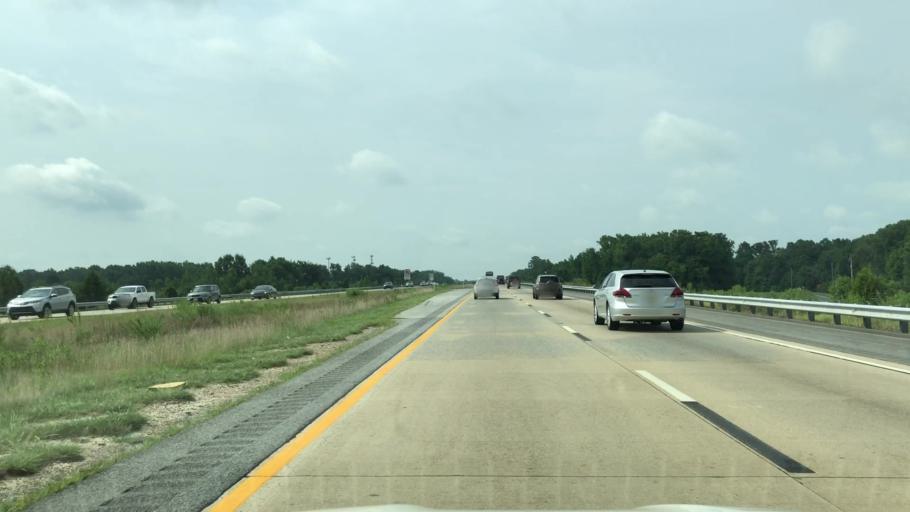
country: US
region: Delaware
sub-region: New Castle County
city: Townsend
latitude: 39.4110
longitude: -75.6618
